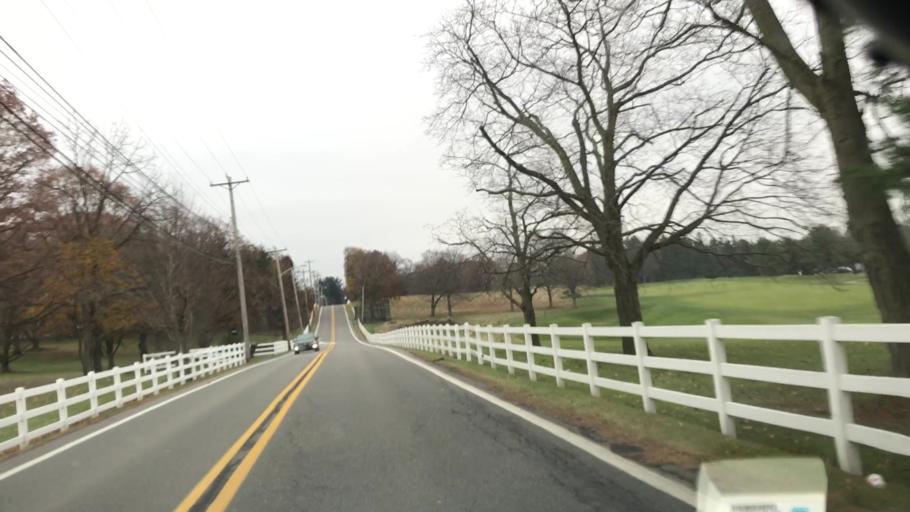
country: US
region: Pennsylvania
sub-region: Allegheny County
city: Carnot-Moon
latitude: 40.5041
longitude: -80.1942
